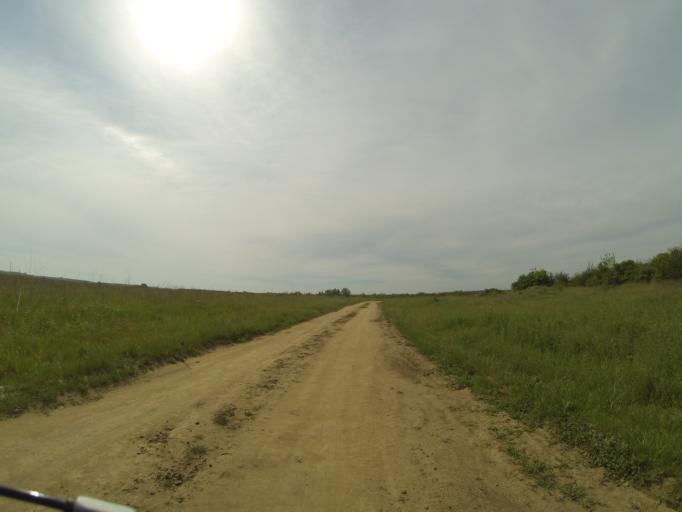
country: RO
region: Dolj
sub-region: Comuna Malu Mare
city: Preajba
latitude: 44.2660
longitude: 23.8639
